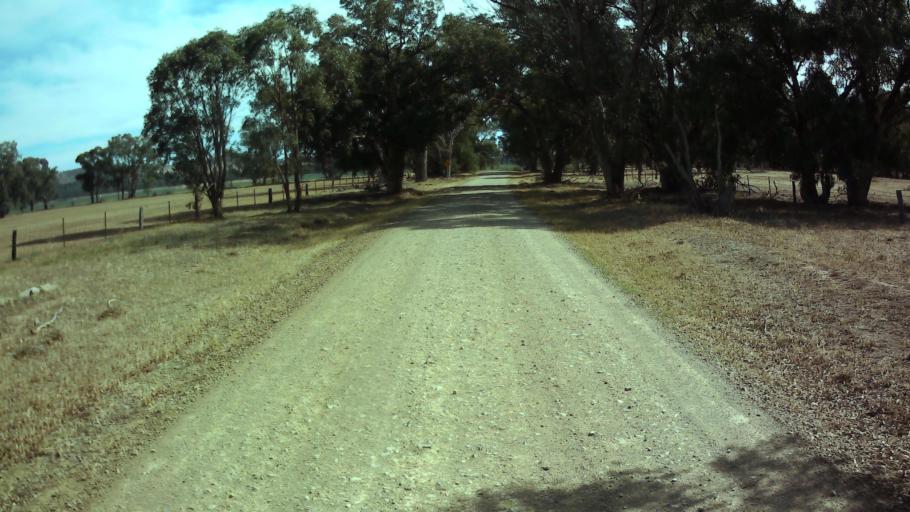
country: AU
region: New South Wales
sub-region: Weddin
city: Grenfell
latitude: -33.6889
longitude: 148.3047
